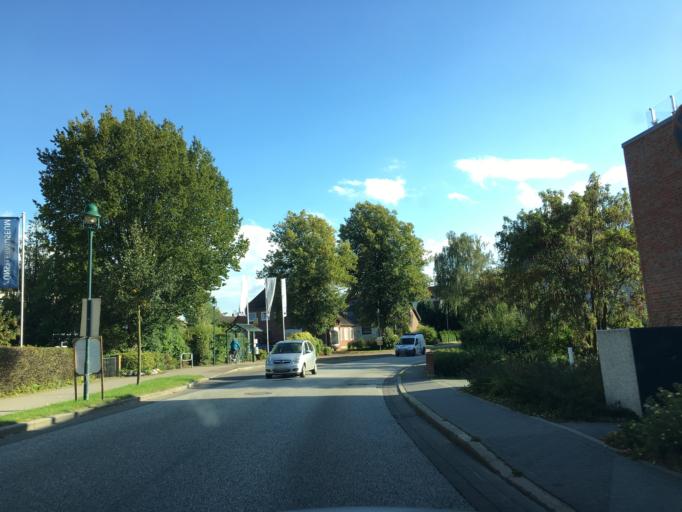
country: DE
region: Schleswig-Holstein
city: Heikendorf
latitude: 54.3681
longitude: 10.2032
